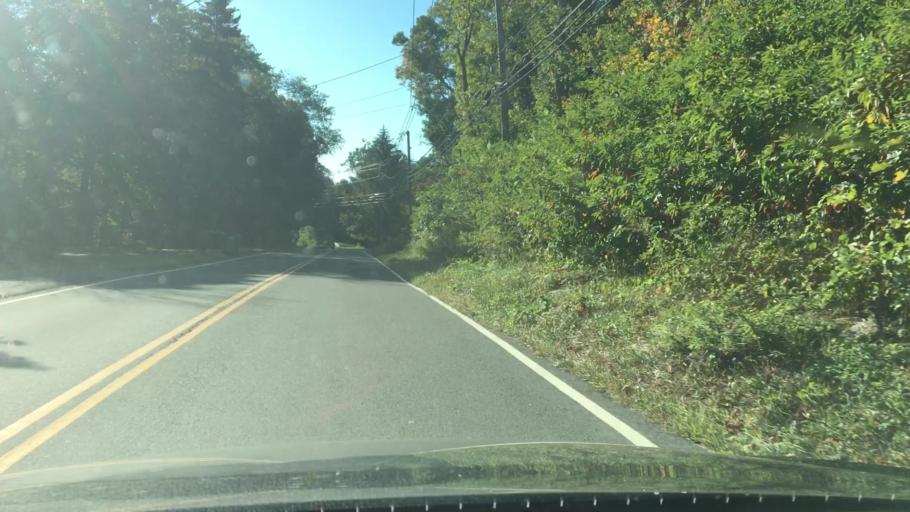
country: US
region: Connecticut
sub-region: New Haven County
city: Ansonia
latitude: 41.3608
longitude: -73.1147
